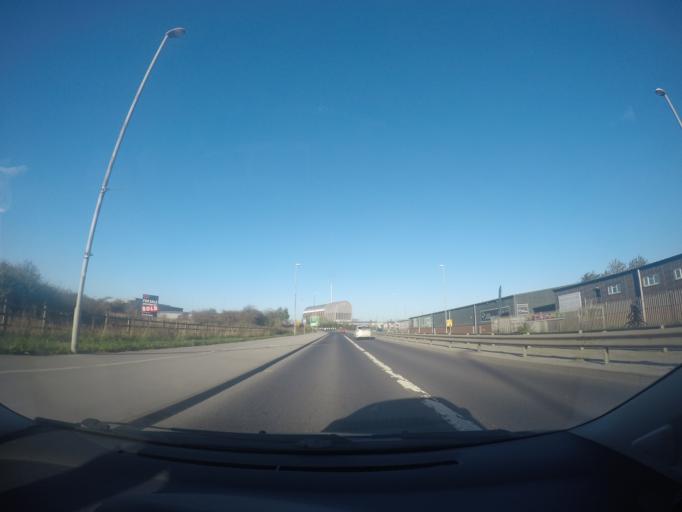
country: GB
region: England
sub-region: City and Borough of Leeds
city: Leeds
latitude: 53.7855
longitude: -1.4967
